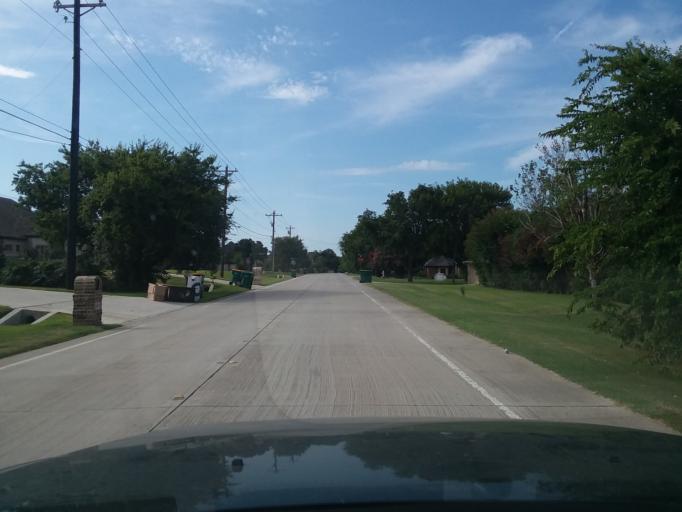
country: US
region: Texas
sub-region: Denton County
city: Double Oak
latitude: 33.0615
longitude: -97.1143
